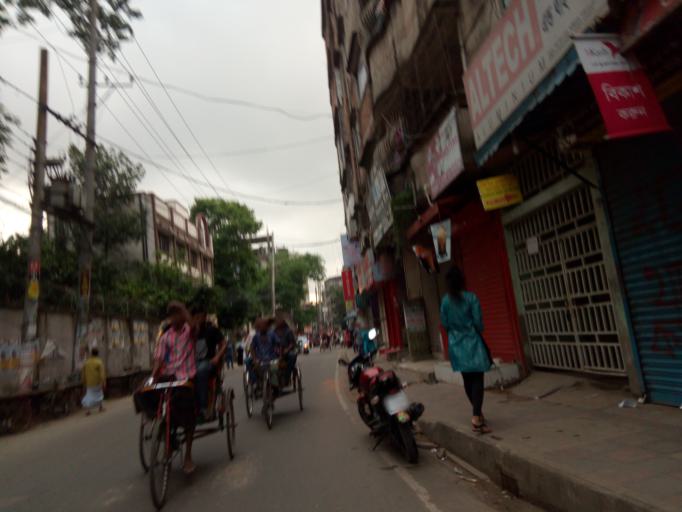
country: BD
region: Dhaka
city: Azimpur
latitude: 23.7264
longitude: 90.3814
